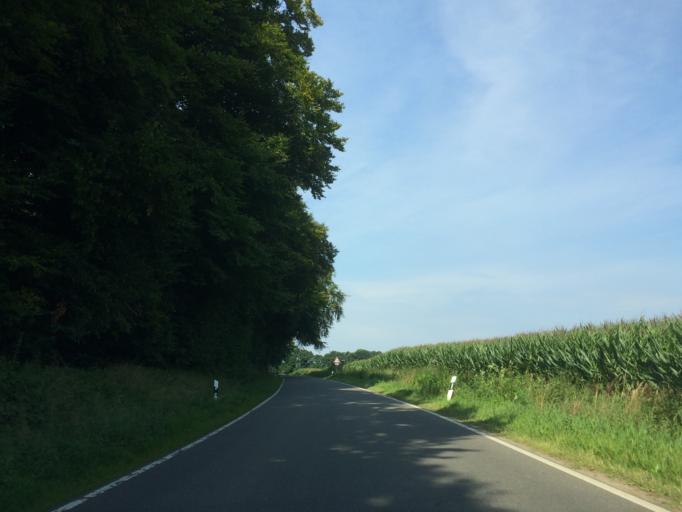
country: DE
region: Schleswig-Holstein
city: Altenhof
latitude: 54.4313
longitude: 9.8926
